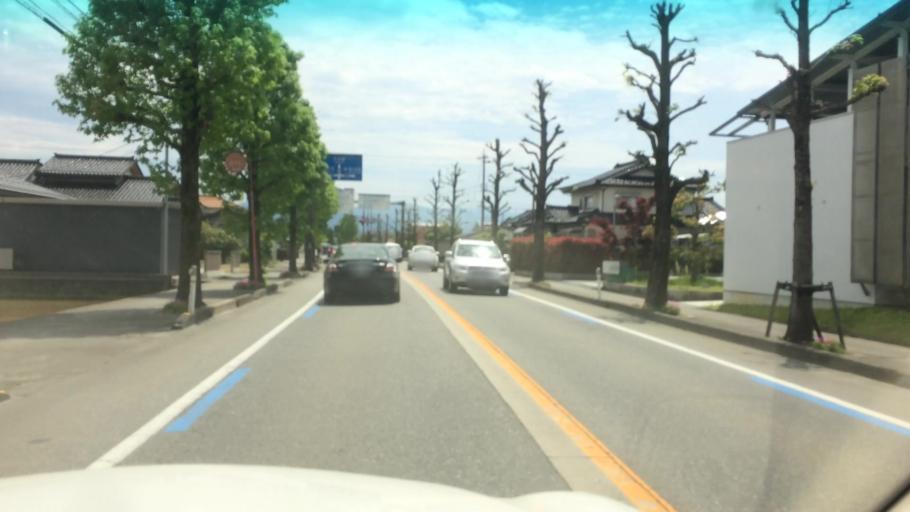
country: JP
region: Toyama
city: Toyama-shi
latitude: 36.6449
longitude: 137.1939
